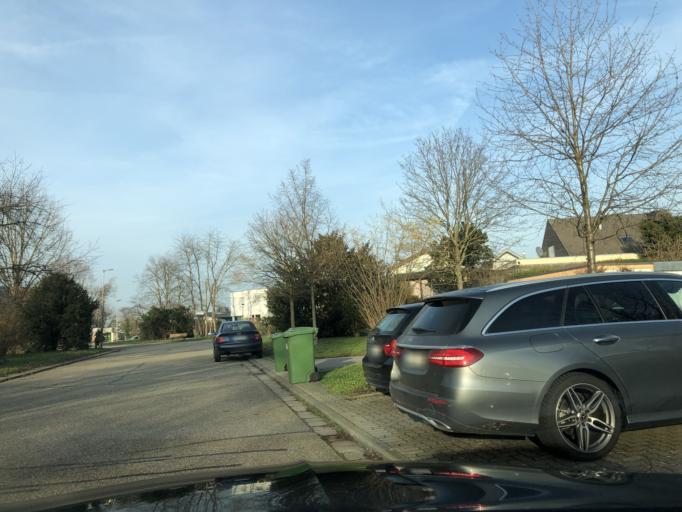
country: DE
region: Baden-Wuerttemberg
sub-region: Karlsruhe Region
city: Ettlingen
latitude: 48.9269
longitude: 8.3621
